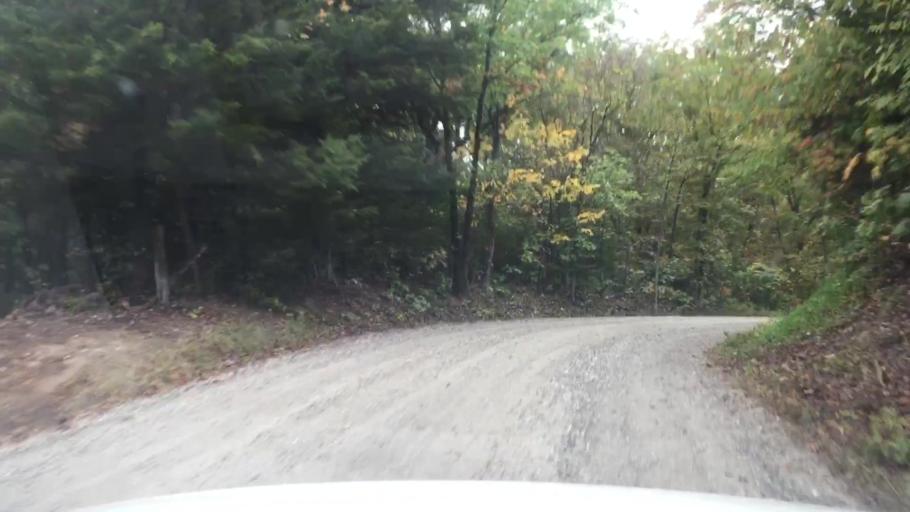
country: US
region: Missouri
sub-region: Boone County
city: Ashland
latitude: 38.8194
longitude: -92.3217
